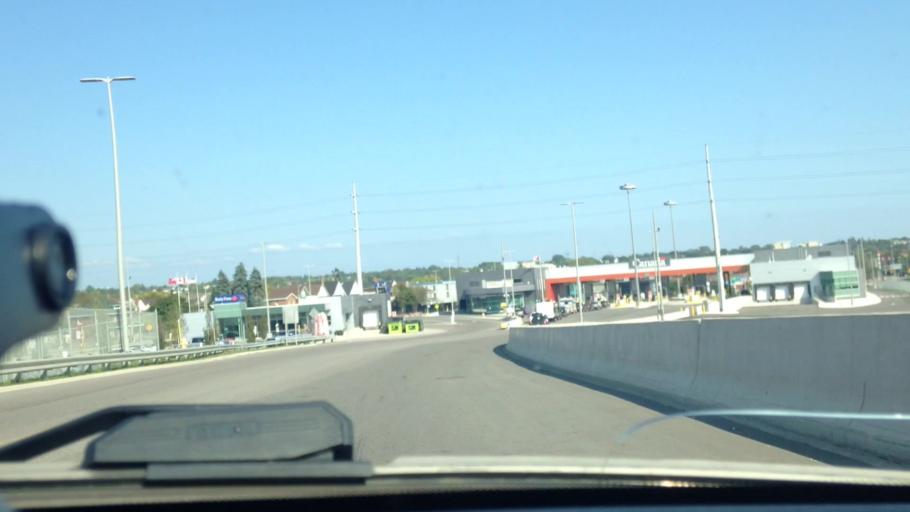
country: CA
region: Ontario
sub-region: Algoma
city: Sault Ste. Marie
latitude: 46.5191
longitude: -84.3525
